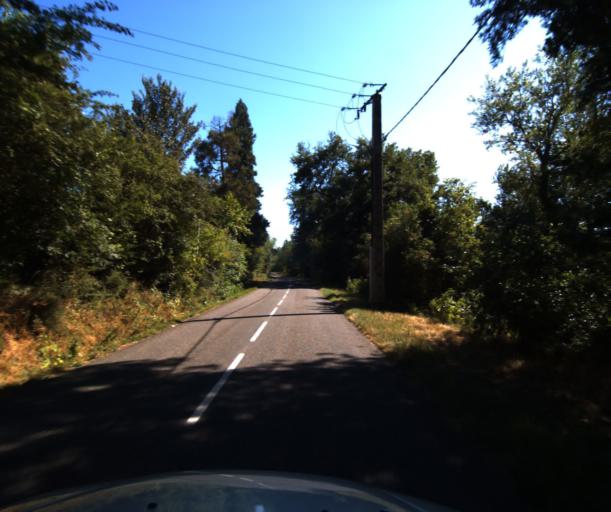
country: FR
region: Midi-Pyrenees
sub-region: Departement de la Haute-Garonne
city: Eaunes
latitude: 43.4388
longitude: 1.3273
